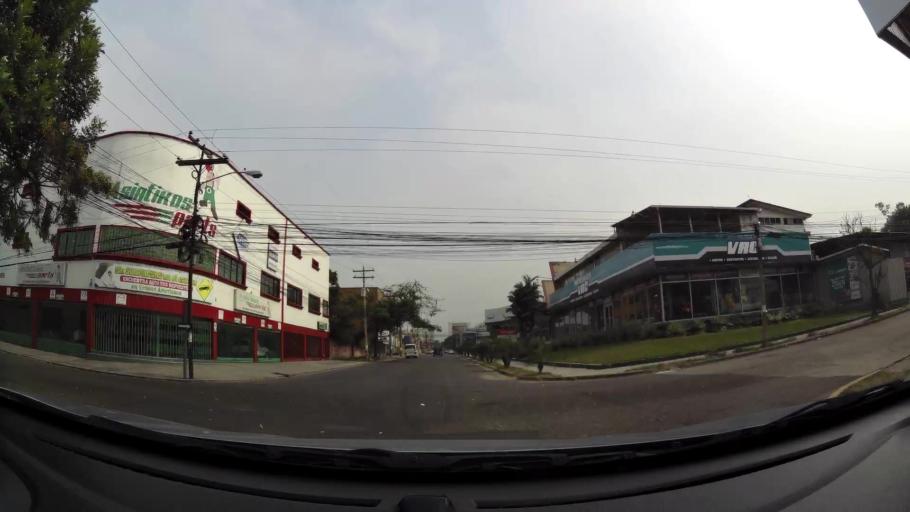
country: HN
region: Cortes
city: San Pedro Sula
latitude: 15.5130
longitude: -88.0238
